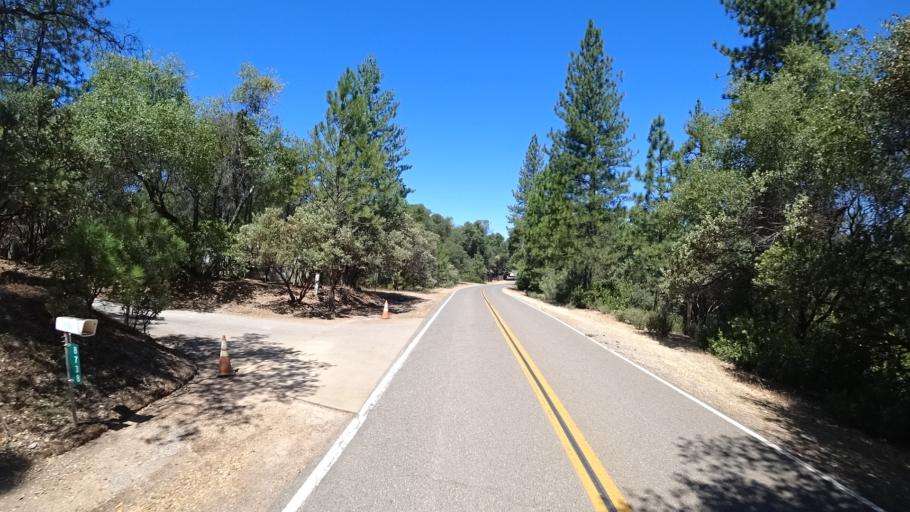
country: US
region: California
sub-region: Calaveras County
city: Mountain Ranch
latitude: 38.2086
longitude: -120.5228
